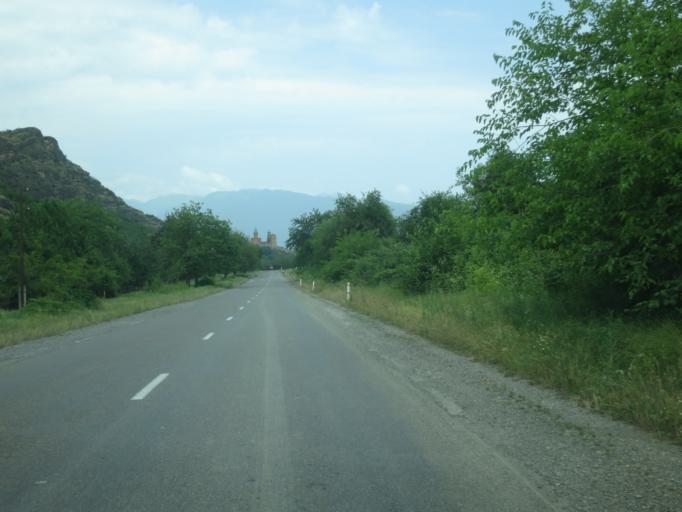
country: GE
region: Kakheti
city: Tsinandali
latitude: 41.9994
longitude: 45.6448
